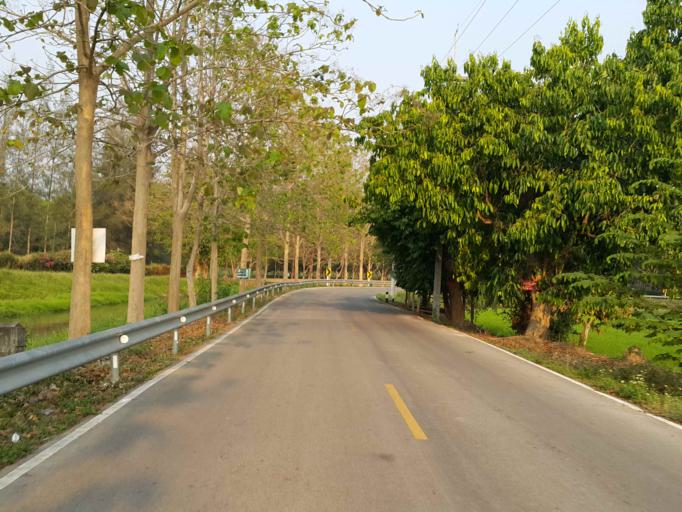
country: TH
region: Chiang Mai
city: Mae Taeng
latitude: 19.0230
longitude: 98.9855
